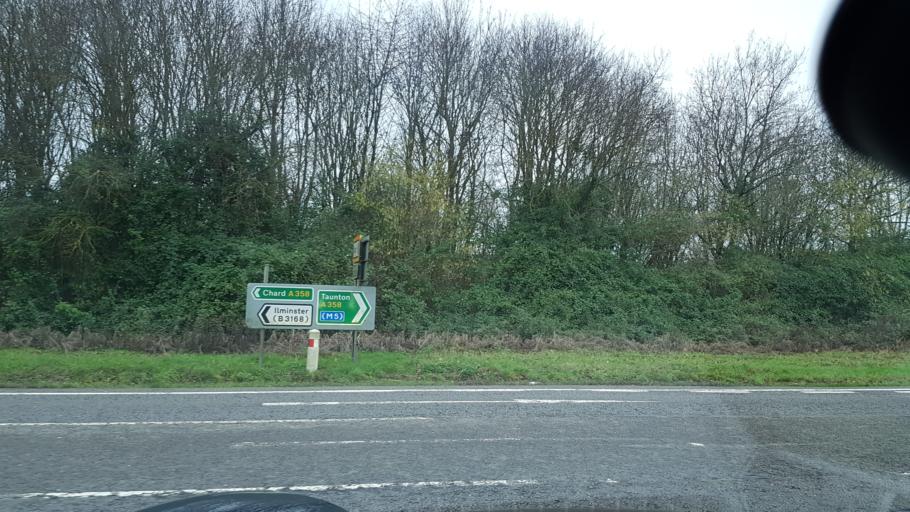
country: GB
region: England
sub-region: Somerset
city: Ilminster
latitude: 50.9504
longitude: -2.9549
